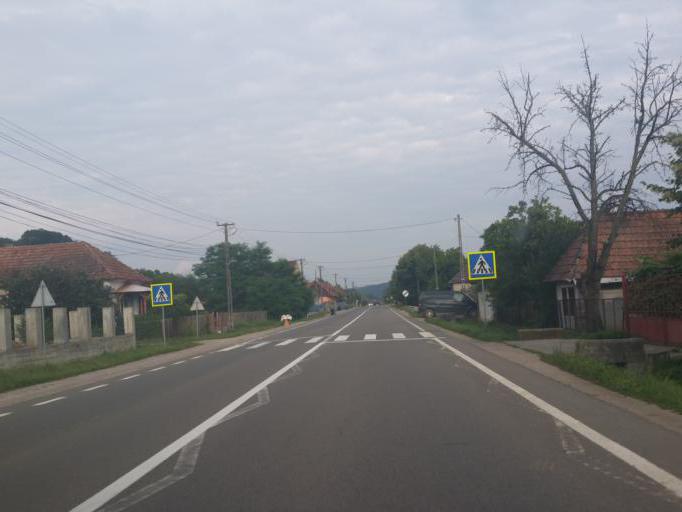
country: RO
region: Salaj
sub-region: Comuna Hida
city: Hida
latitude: 47.0474
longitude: 23.2460
